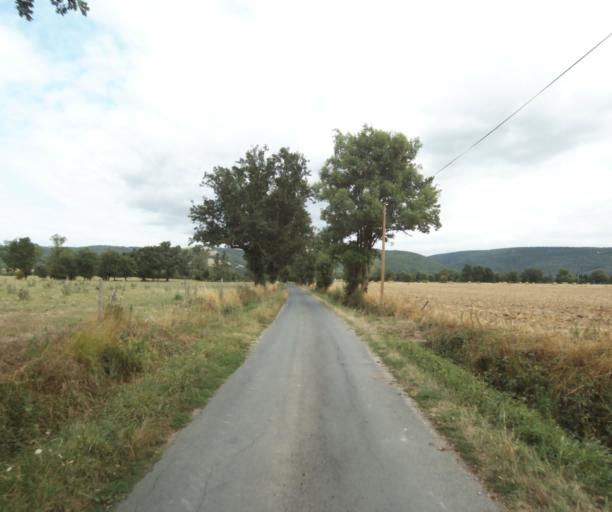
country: FR
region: Midi-Pyrenees
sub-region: Departement du Tarn
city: Soreze
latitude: 43.4627
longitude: 2.0582
